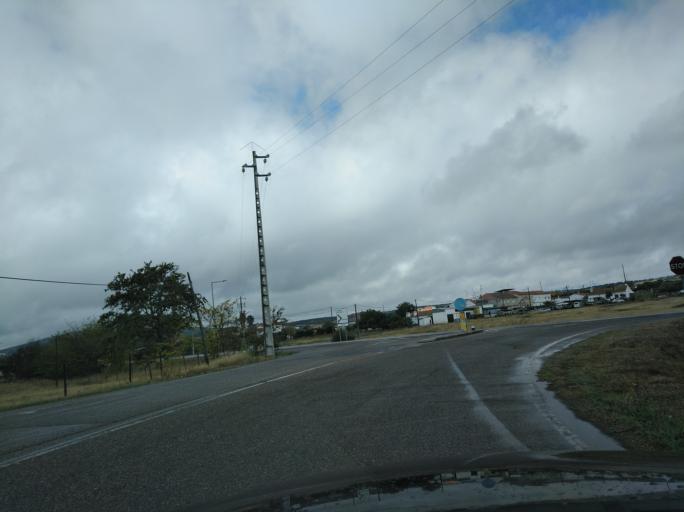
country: PT
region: Portalegre
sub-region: Elvas
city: Elvas
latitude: 38.8880
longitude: -7.1177
